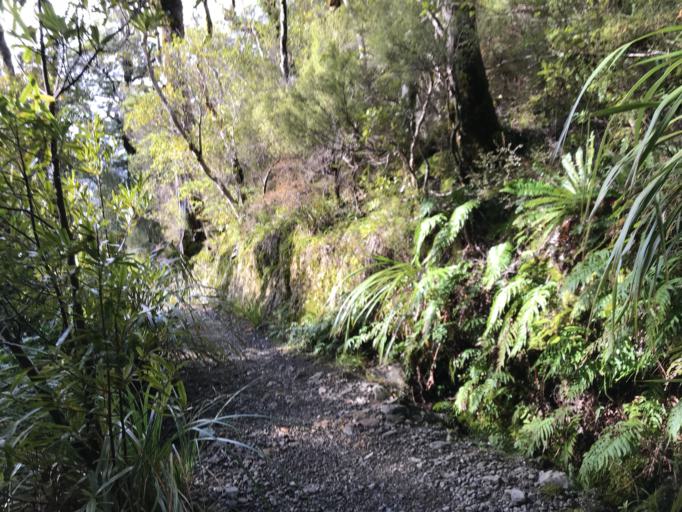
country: NZ
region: Wellington
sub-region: Masterton District
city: Masterton
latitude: -40.9040
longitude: 175.4556
